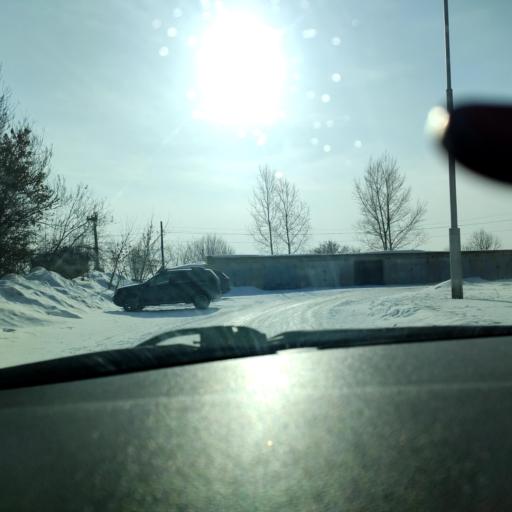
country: RU
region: Bashkortostan
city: Ufa
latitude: 54.5707
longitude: 55.9062
